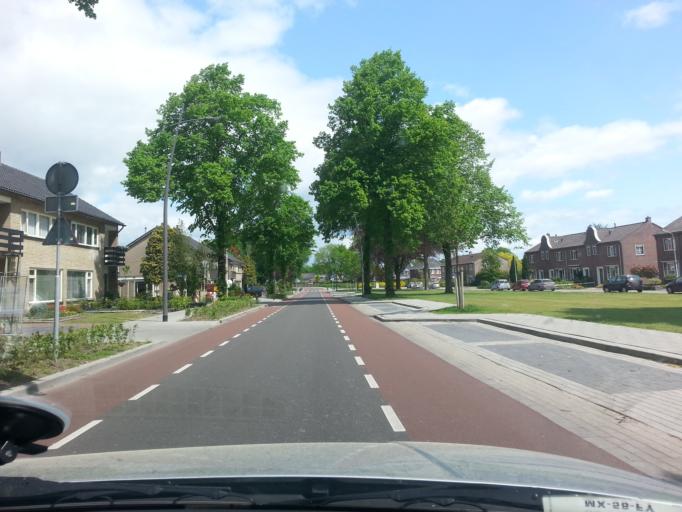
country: NL
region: Overijssel
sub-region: Gemeente Losser
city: Losser
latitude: 52.2665
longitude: 7.0046
